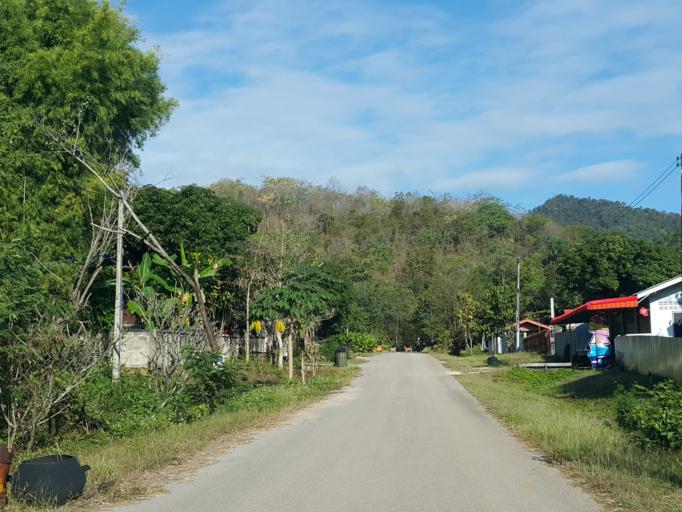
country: TH
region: Lampang
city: Mae Mo
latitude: 18.2826
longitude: 99.6415
